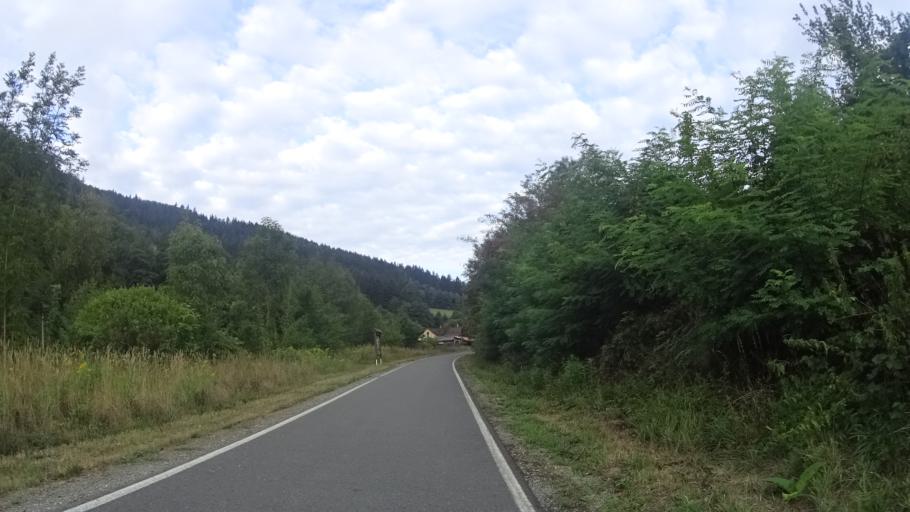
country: CZ
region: Olomoucky
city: Zabreh
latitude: 49.8634
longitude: 16.8130
